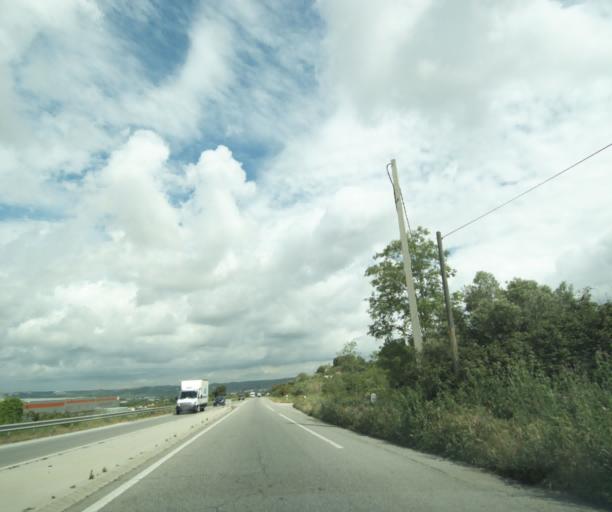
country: FR
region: Provence-Alpes-Cote d'Azur
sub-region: Departement des Bouches-du-Rhone
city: La Fare-les-Oliviers
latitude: 43.5205
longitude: 5.1991
